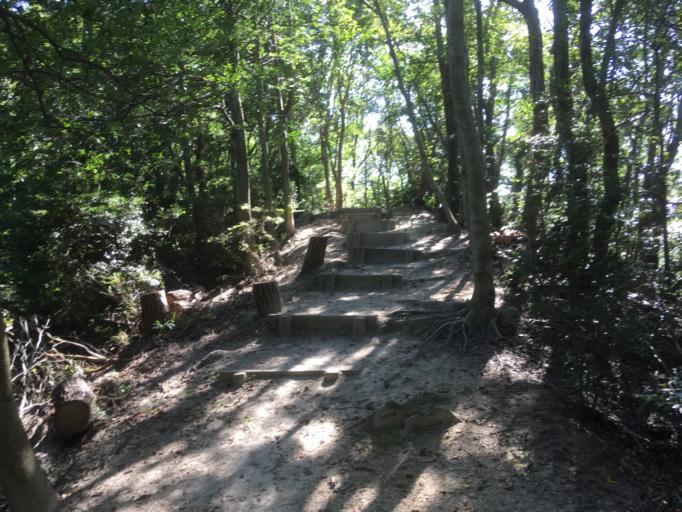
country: JP
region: Nara
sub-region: Ikoma-shi
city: Ikoma
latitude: 34.7198
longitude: 135.6709
